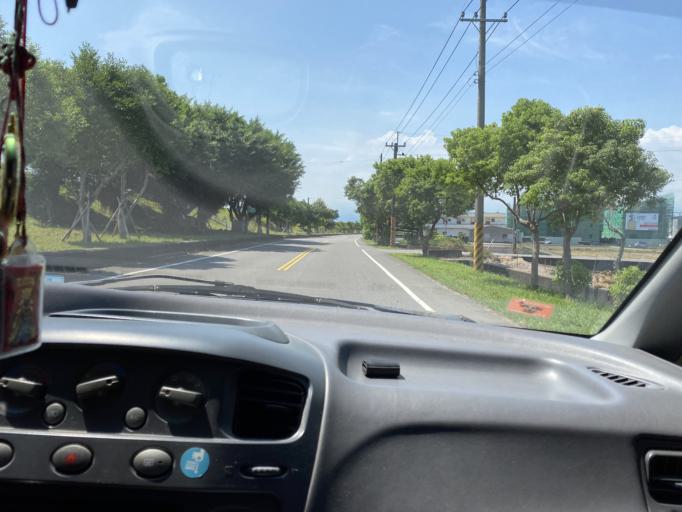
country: TW
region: Taiwan
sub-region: Yilan
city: Yilan
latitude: 24.7190
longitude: 121.7960
